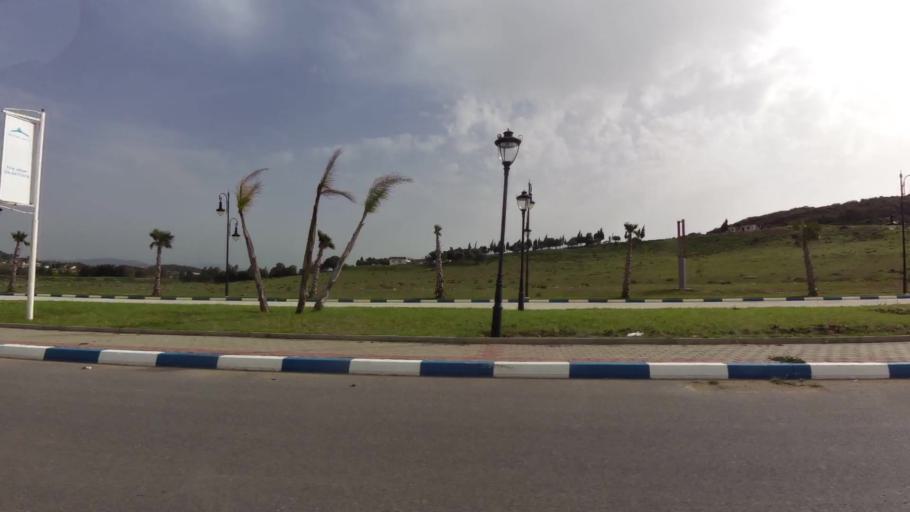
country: MA
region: Tanger-Tetouan
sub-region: Tanger-Assilah
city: Boukhalef
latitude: 35.6970
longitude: -5.9217
